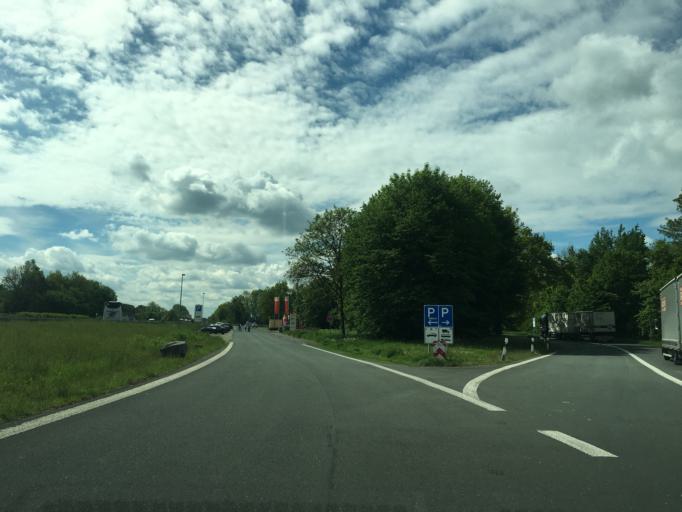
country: DE
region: North Rhine-Westphalia
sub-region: Regierungsbezirk Munster
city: Ascheberg
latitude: 51.7751
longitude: 7.6393
